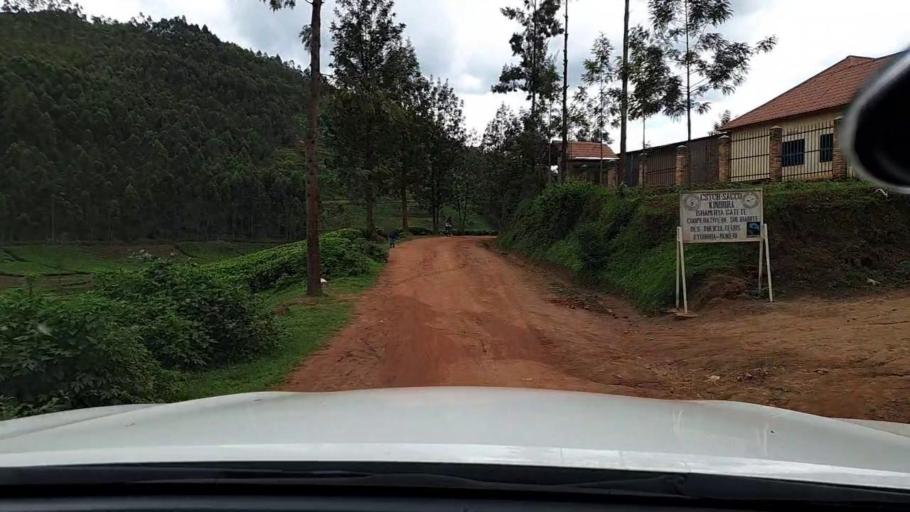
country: RW
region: Northern Province
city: Byumba
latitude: -1.6577
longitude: 29.9110
